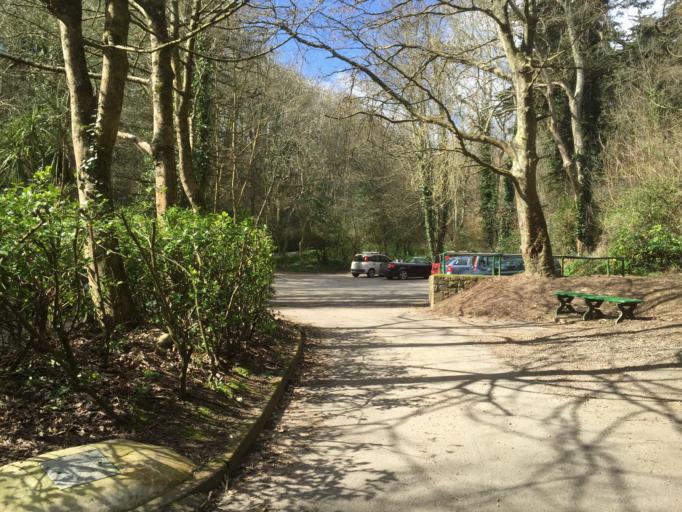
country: GG
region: St Peter Port
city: Saint Peter Port
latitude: 49.4278
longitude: -2.5513
